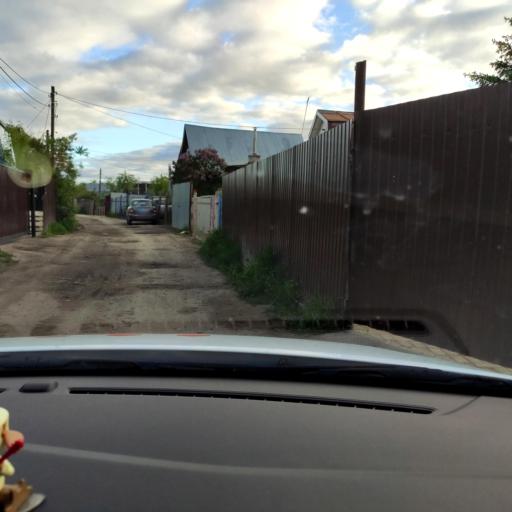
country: RU
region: Tatarstan
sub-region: Gorod Kazan'
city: Kazan
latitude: 55.8459
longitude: 49.1944
